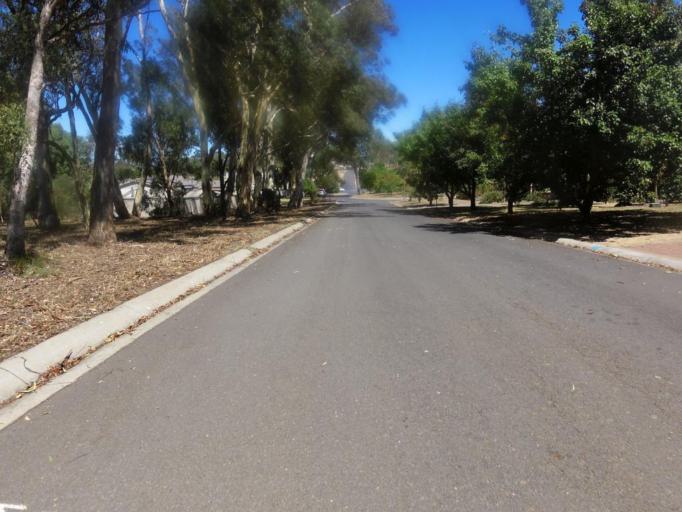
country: AU
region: Victoria
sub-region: Mount Alexander
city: Castlemaine
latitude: -37.0673
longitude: 144.1944
